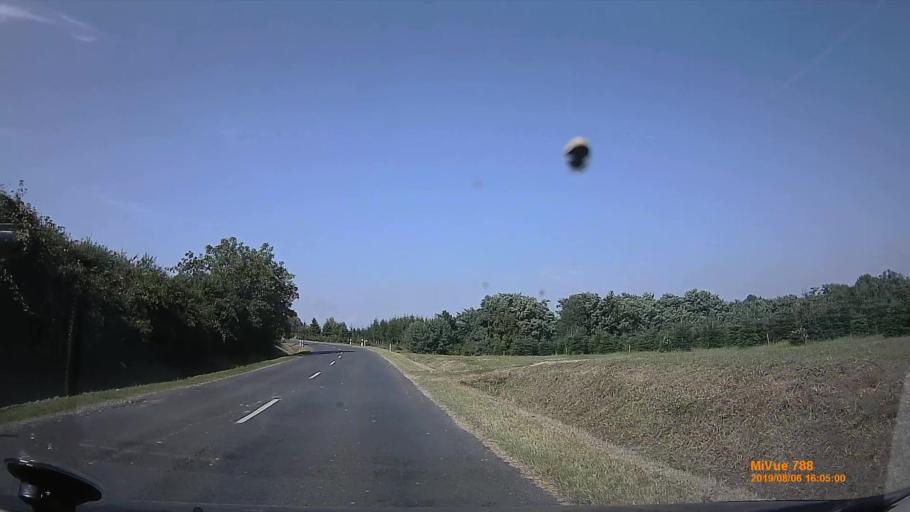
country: HU
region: Zala
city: Murakeresztur
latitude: 46.3086
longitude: 16.9609
